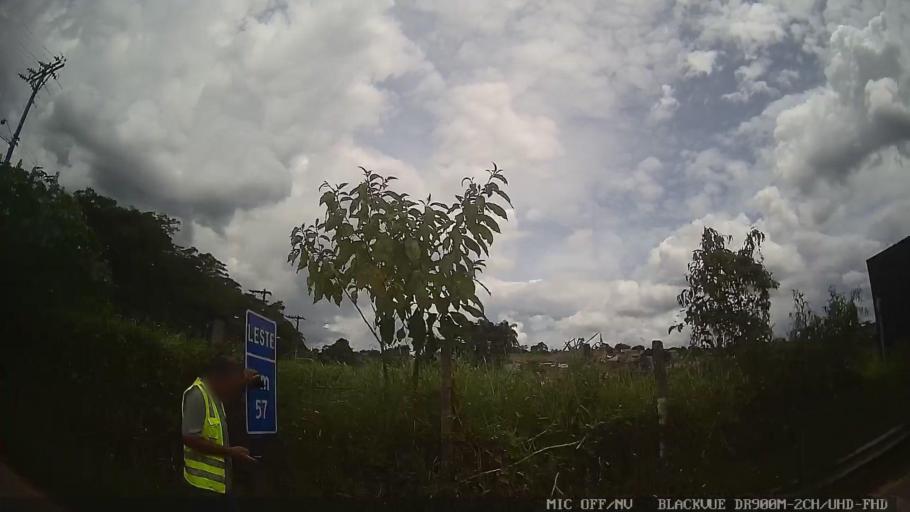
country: BR
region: Sao Paulo
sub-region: Ribeirao Pires
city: Ribeirao Pires
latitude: -23.6578
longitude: -46.3317
